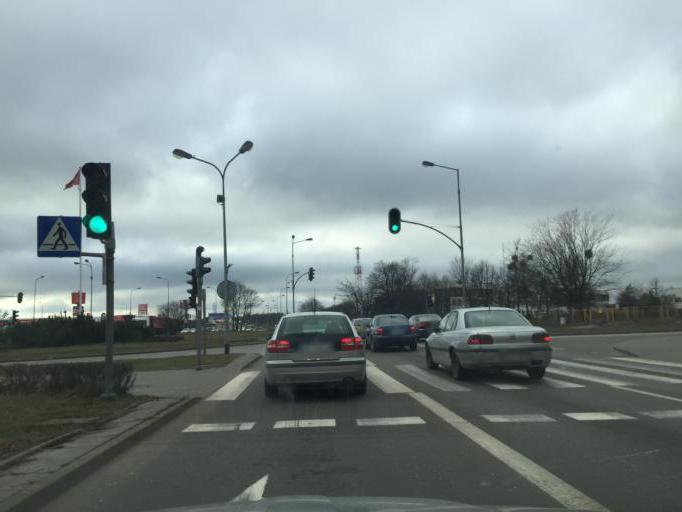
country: PL
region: Pomeranian Voivodeship
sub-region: Sopot
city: Sopot
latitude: 54.3765
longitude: 18.5230
